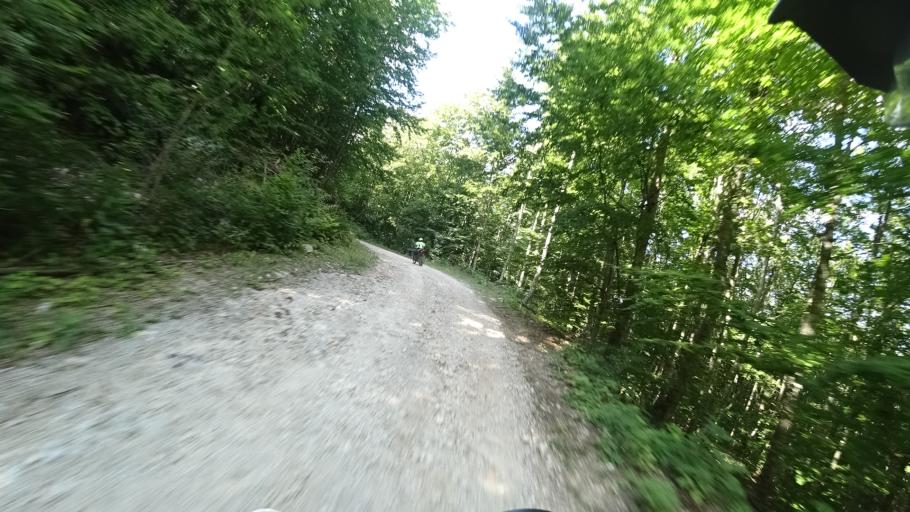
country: HR
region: Zadarska
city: Gracac
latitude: 44.4501
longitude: 15.9816
